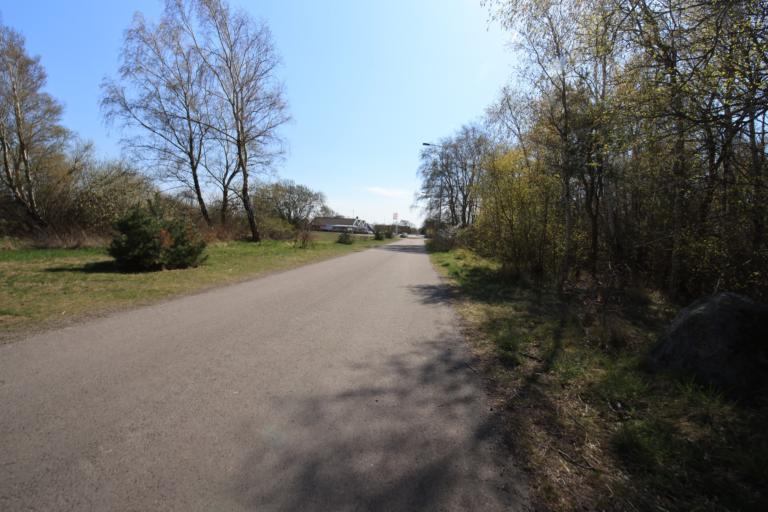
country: SE
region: Halland
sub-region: Varbergs Kommun
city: Traslovslage
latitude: 57.0555
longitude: 12.2860
